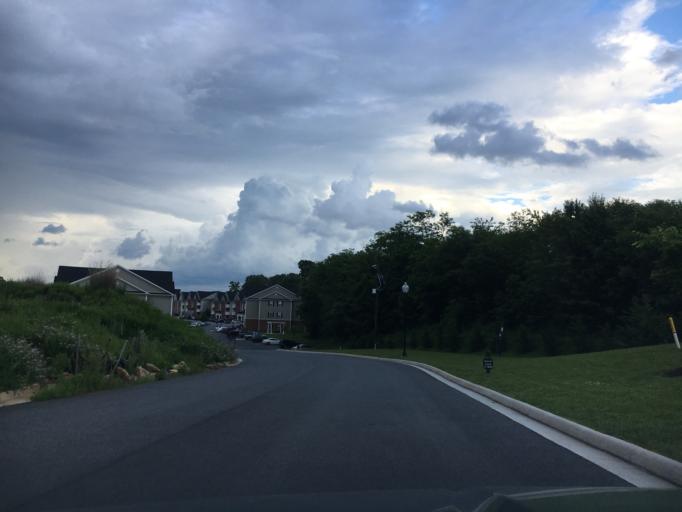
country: US
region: Virginia
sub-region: Bedford County
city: Forest
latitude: 37.3681
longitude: -79.2587
